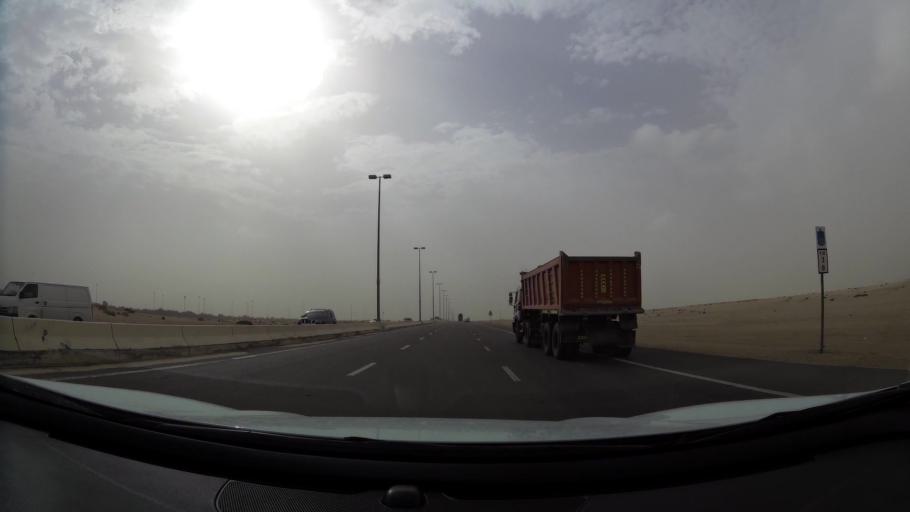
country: AE
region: Abu Dhabi
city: Abu Dhabi
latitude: 24.4699
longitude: 54.6715
